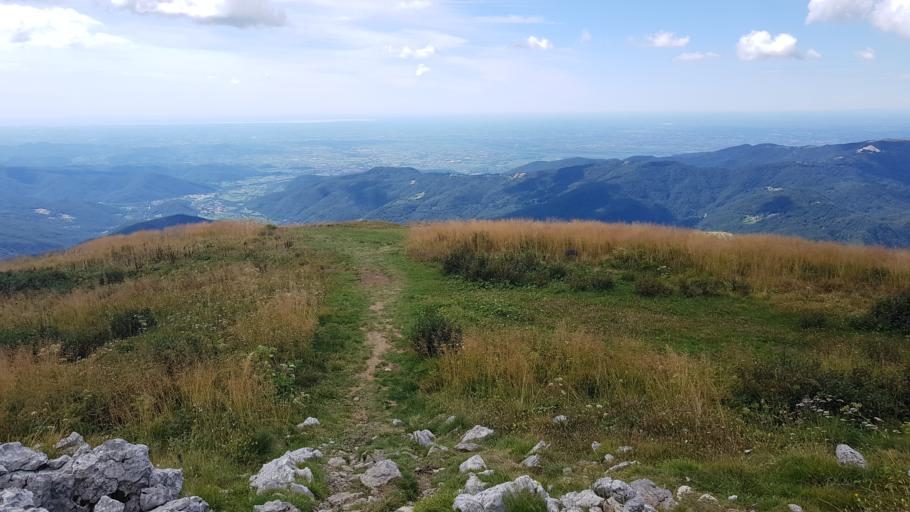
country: IT
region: Friuli Venezia Giulia
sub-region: Provincia di Udine
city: Savogna
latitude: 46.2116
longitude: 13.5291
